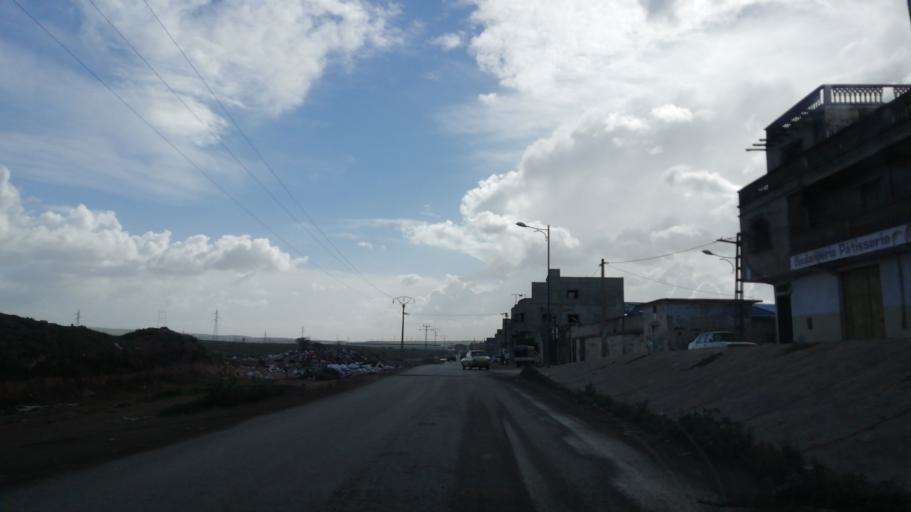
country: DZ
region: Oran
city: Sidi ech Chahmi
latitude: 35.6473
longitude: -0.5610
